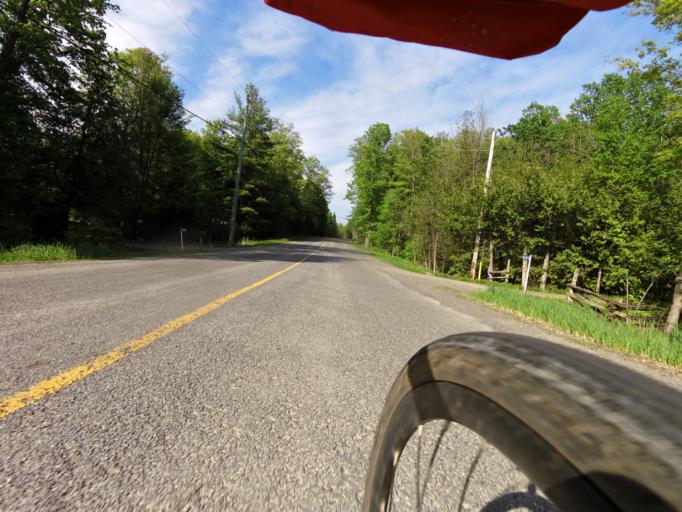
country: CA
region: Ontario
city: Arnprior
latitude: 45.1694
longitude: -76.4762
